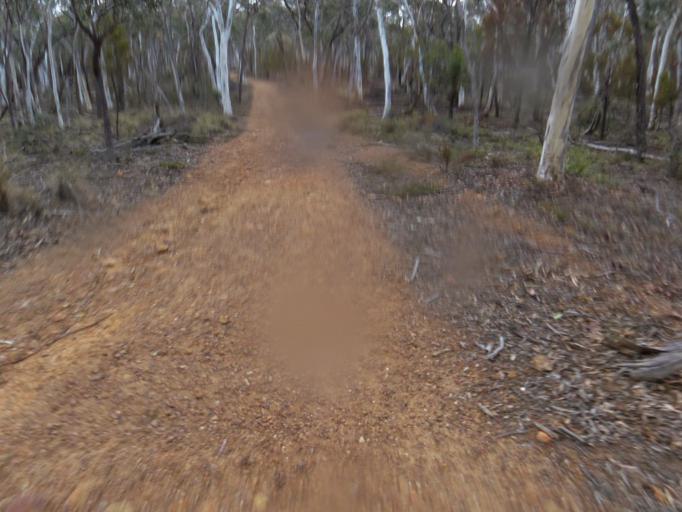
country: AU
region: Australian Capital Territory
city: Acton
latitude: -35.2661
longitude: 149.0981
